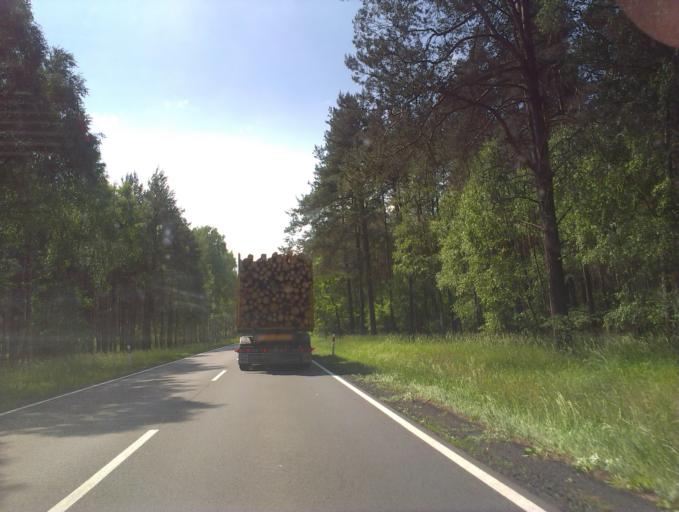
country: PL
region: Greater Poland Voivodeship
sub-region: Powiat zlotowski
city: Tarnowka
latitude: 53.3343
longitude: 16.7930
